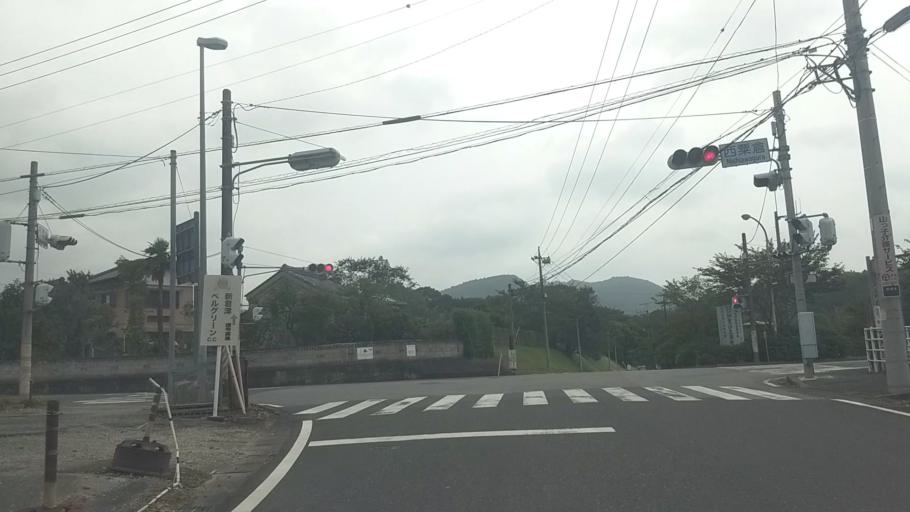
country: JP
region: Chiba
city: Kimitsu
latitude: 35.2521
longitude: 139.9944
